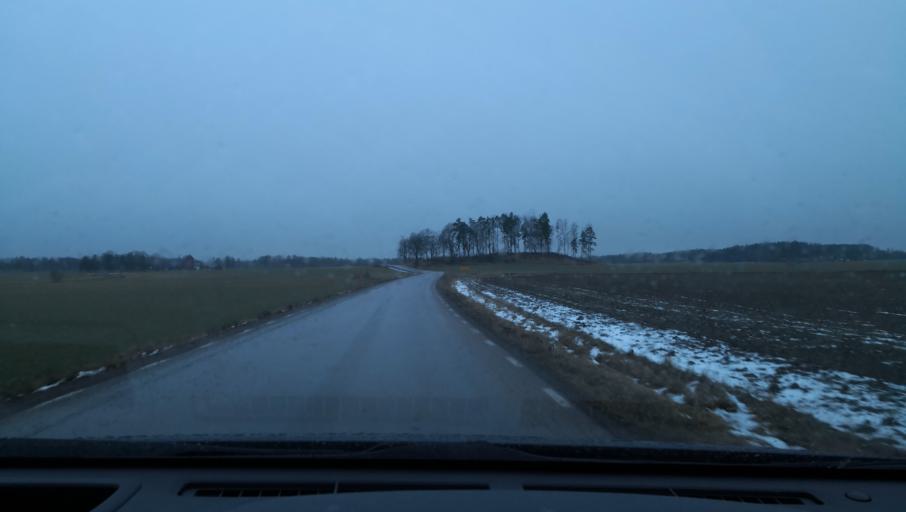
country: SE
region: Soedermanland
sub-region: Eskilstuna Kommun
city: Arla
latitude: 59.4343
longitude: 16.7116
